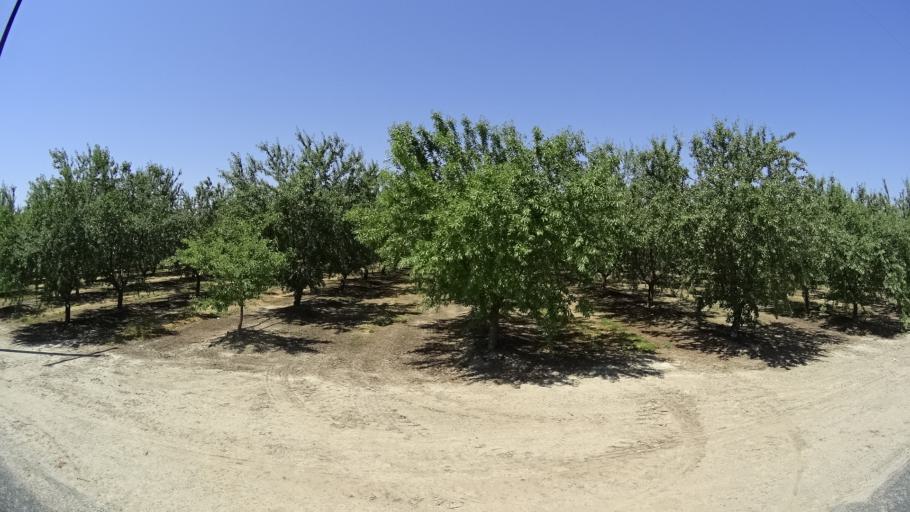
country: US
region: California
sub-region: Kings County
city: Armona
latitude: 36.2640
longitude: -119.7269
